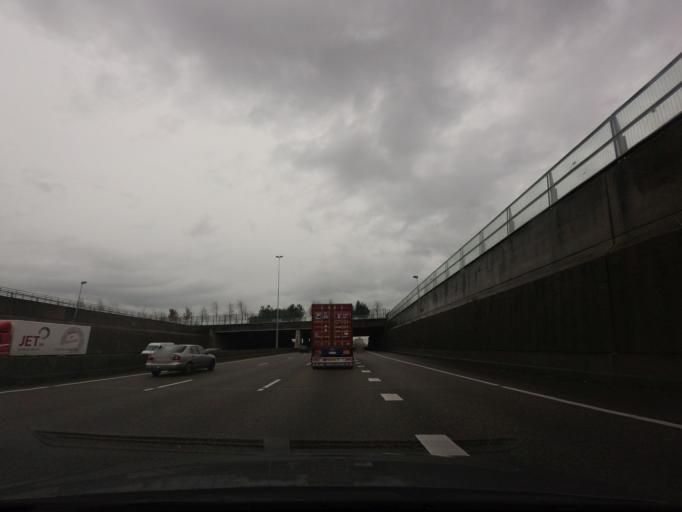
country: NL
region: North Brabant
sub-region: Gemeente Breda
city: Breda
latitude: 51.5968
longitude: 4.7233
